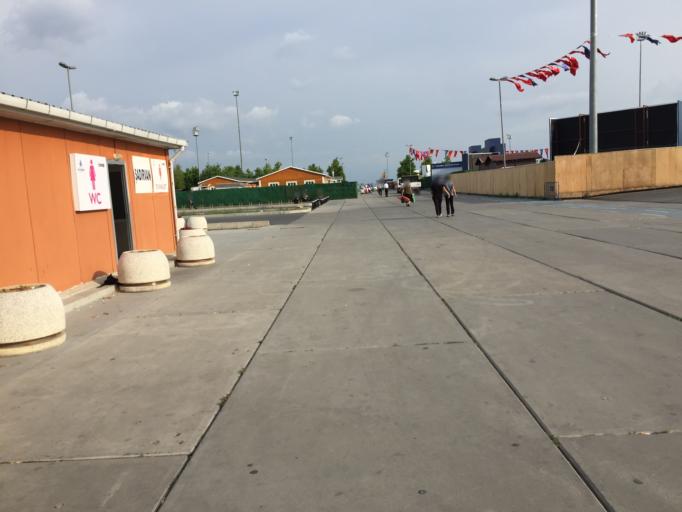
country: TR
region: Istanbul
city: Istanbul
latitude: 41.0002
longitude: 28.9397
